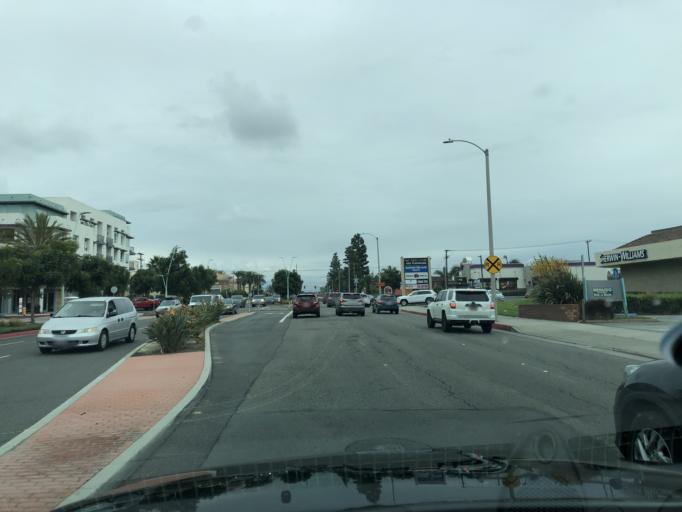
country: US
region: California
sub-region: Orange County
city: Midway City
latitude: 33.7301
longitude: -117.9995
